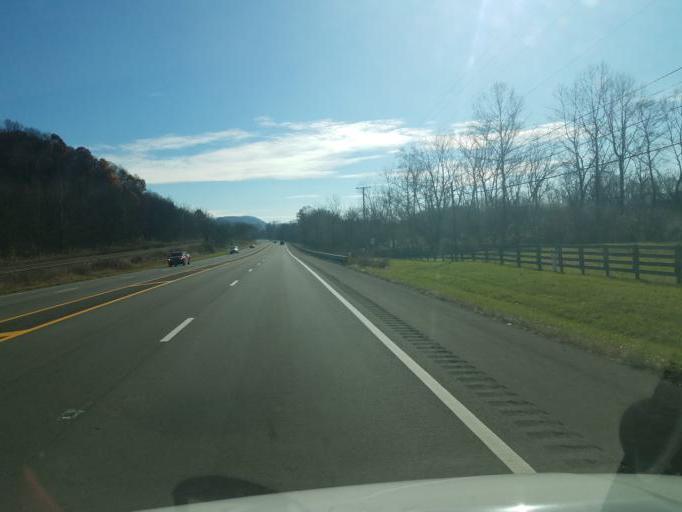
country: US
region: Ohio
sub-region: Scioto County
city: Lucasville
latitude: 38.8502
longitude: -82.9866
